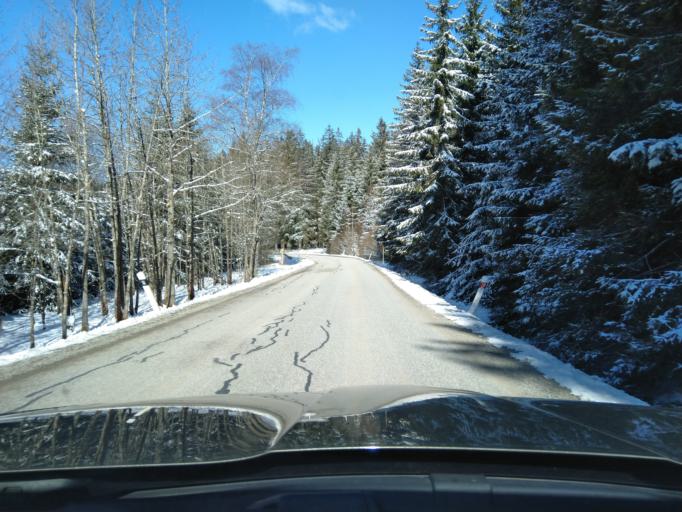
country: CZ
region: Jihocesky
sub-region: Okres Prachatice
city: Zdikov
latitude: 49.0475
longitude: 13.6693
